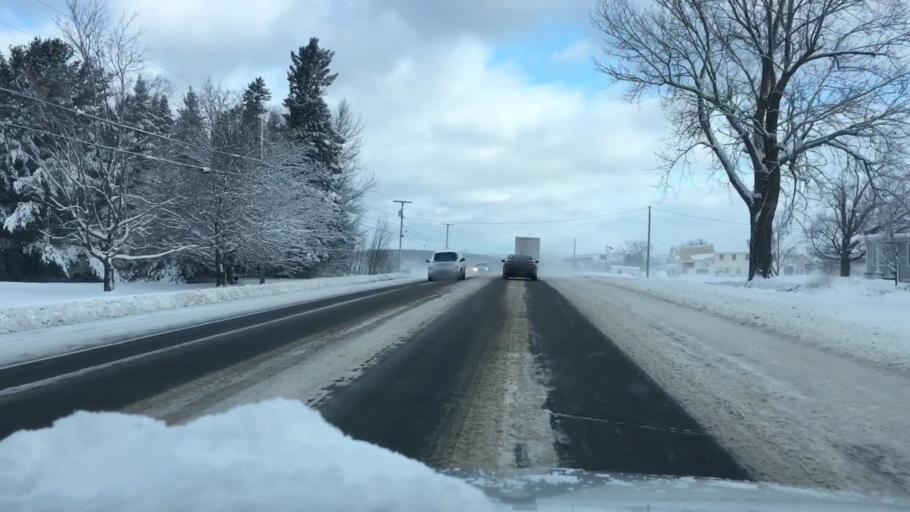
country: US
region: Maine
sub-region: Aroostook County
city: Caribou
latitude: 46.7932
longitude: -67.9913
